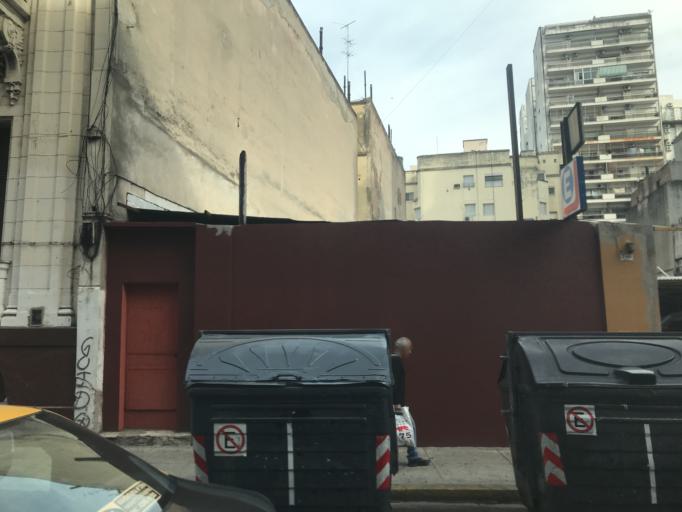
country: AR
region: Buenos Aires F.D.
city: Buenos Aires
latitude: -34.6260
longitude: -58.3757
